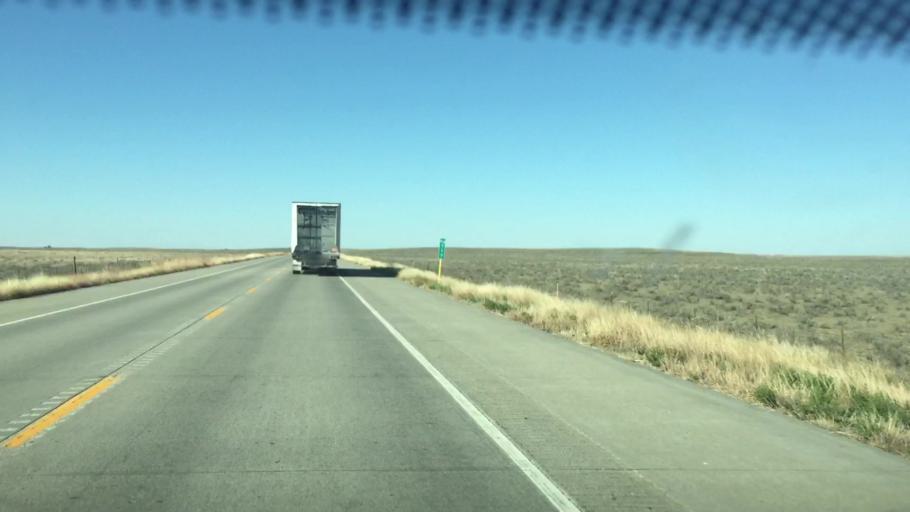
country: US
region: Colorado
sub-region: Kiowa County
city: Eads
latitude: 38.5308
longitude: -102.7857
